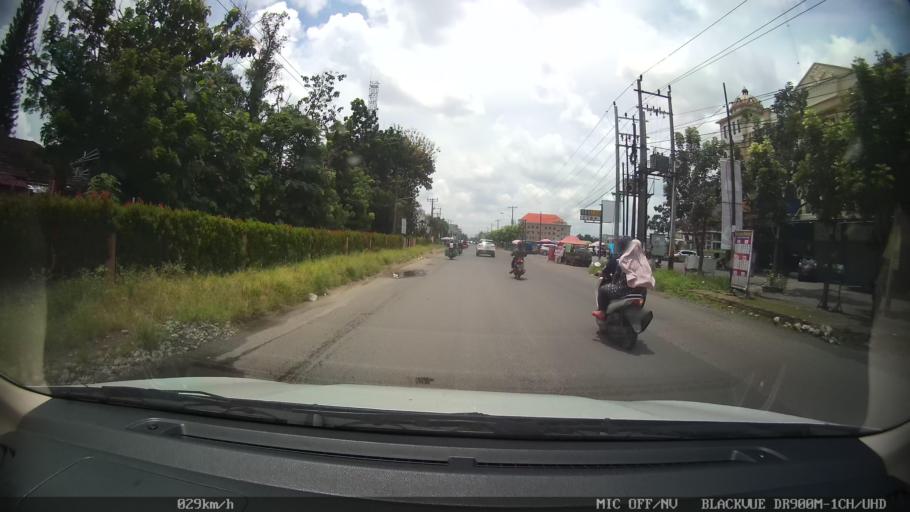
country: ID
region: North Sumatra
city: Medan
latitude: 3.6026
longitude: 98.7119
